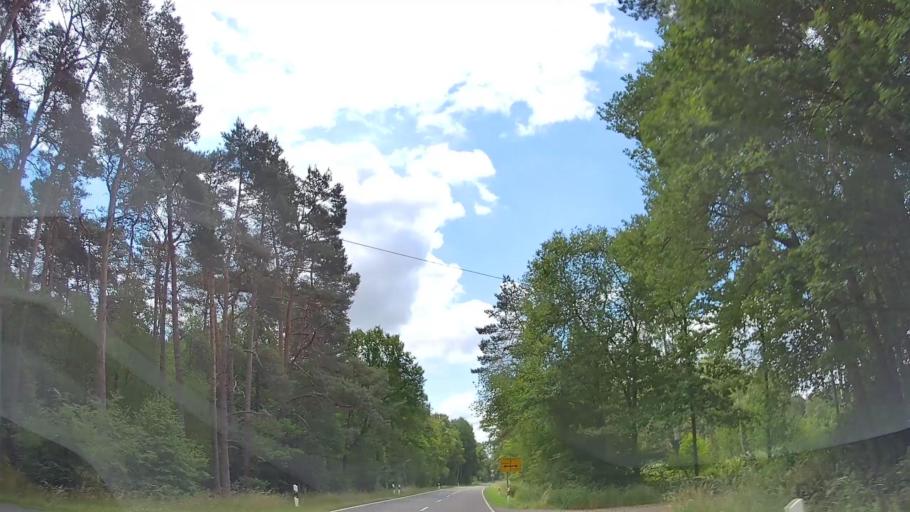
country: DE
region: North Rhine-Westphalia
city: Rahden
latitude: 52.4194
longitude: 8.5193
